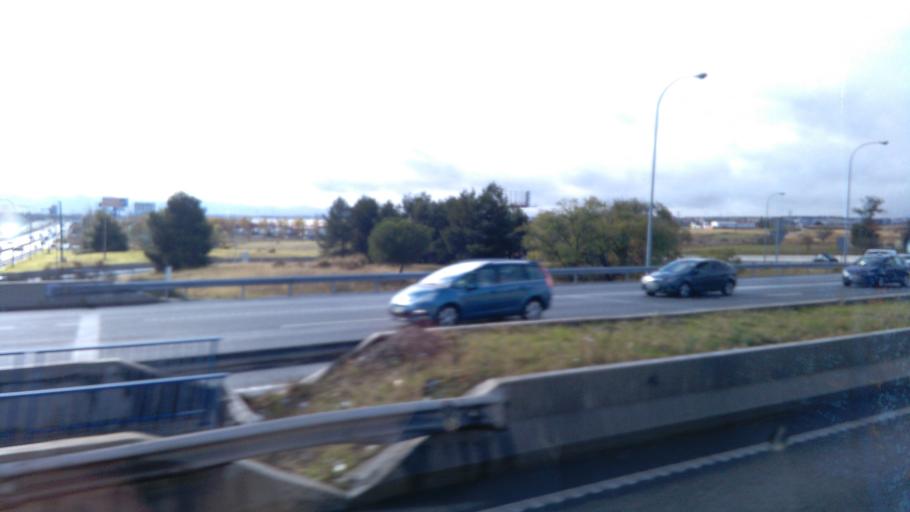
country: ES
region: Madrid
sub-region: Provincia de Madrid
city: Villaverde
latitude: 40.3649
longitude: -3.7210
